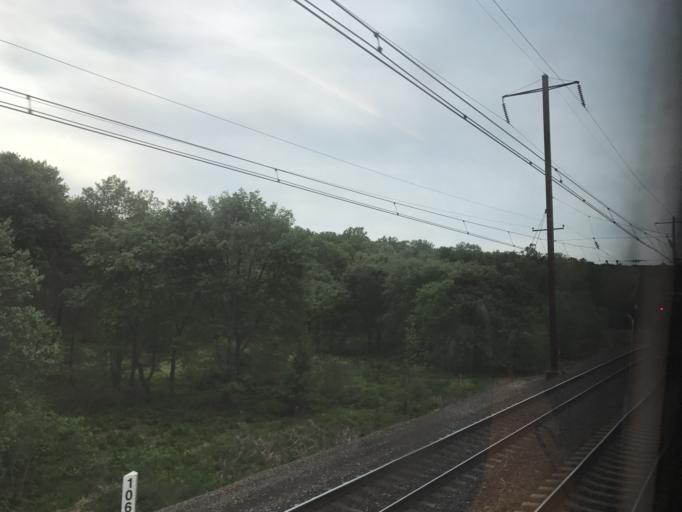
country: US
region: Maryland
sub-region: Howard County
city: Elkridge
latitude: 39.1958
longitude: -76.6960
